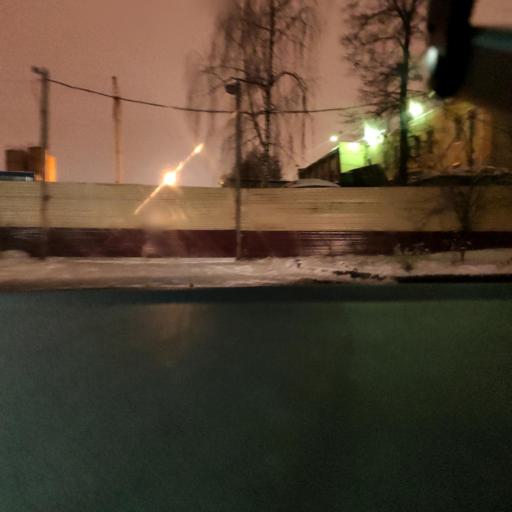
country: RU
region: Moscow
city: Amin'yevo
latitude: 55.7122
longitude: 37.4460
